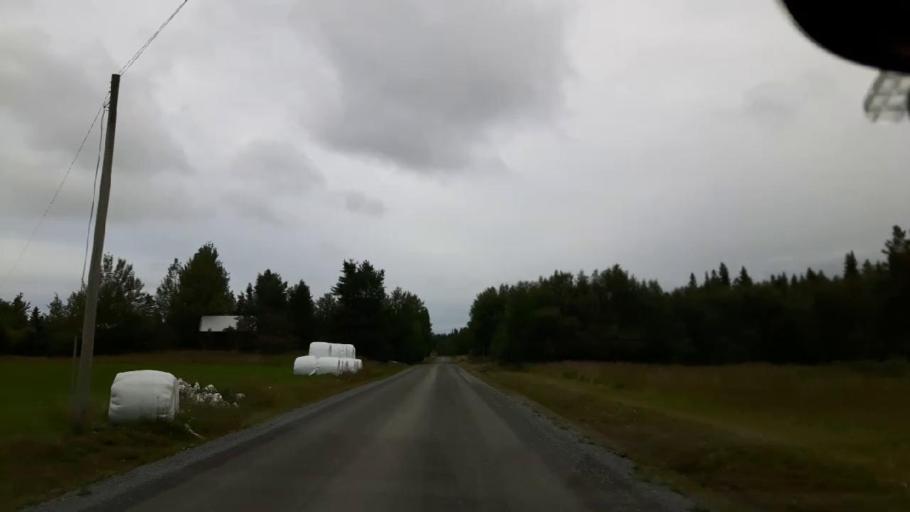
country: SE
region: Jaemtland
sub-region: OEstersunds Kommun
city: Ostersund
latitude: 63.1081
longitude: 14.5458
